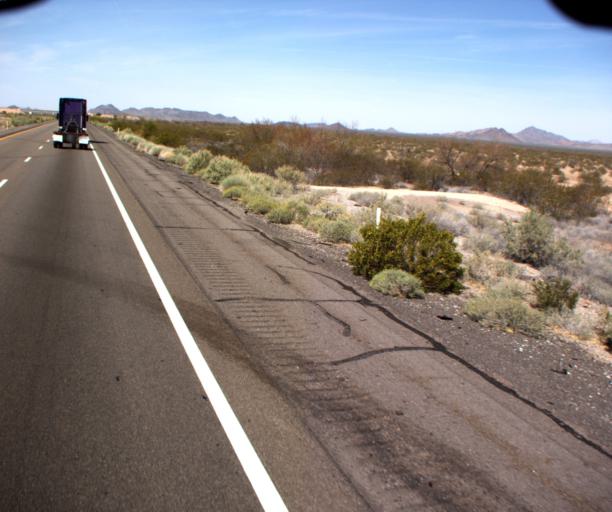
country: US
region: Arizona
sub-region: La Paz County
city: Salome
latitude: 33.5938
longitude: -113.5154
